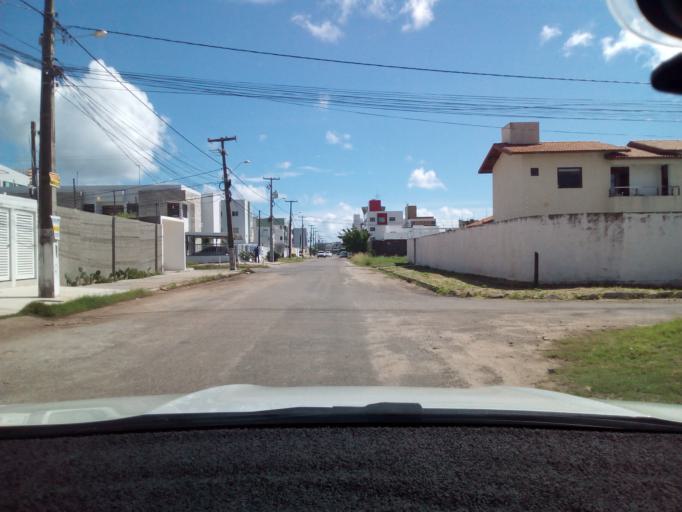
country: BR
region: Paraiba
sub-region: Joao Pessoa
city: Joao Pessoa
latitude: -7.0550
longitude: -34.8495
